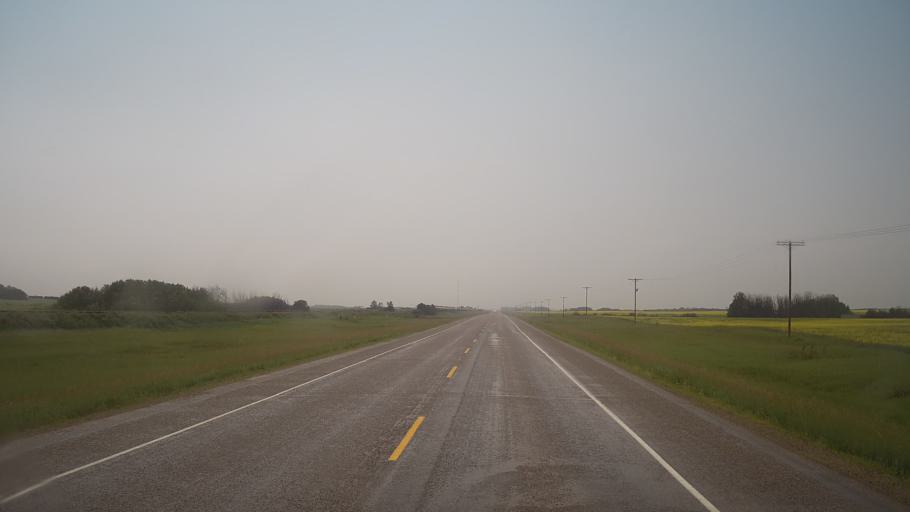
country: CA
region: Saskatchewan
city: Biggar
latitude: 52.1638
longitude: -108.2935
